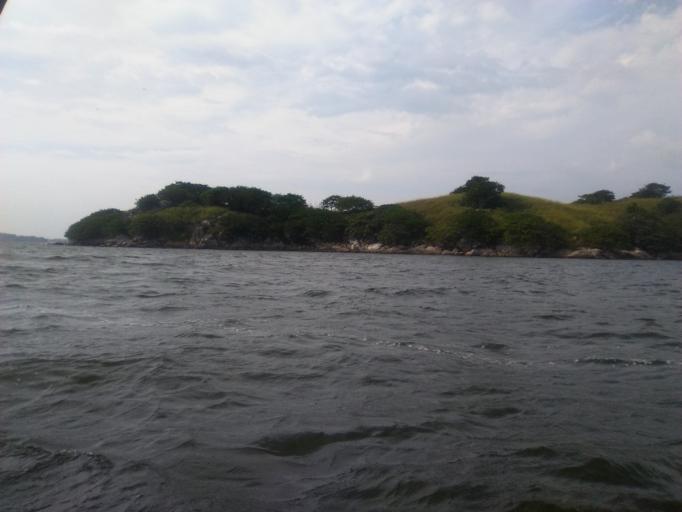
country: MX
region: Guerrero
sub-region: Coyuca de Benitez
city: El Embarcadero
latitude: 16.9495
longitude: -100.0166
